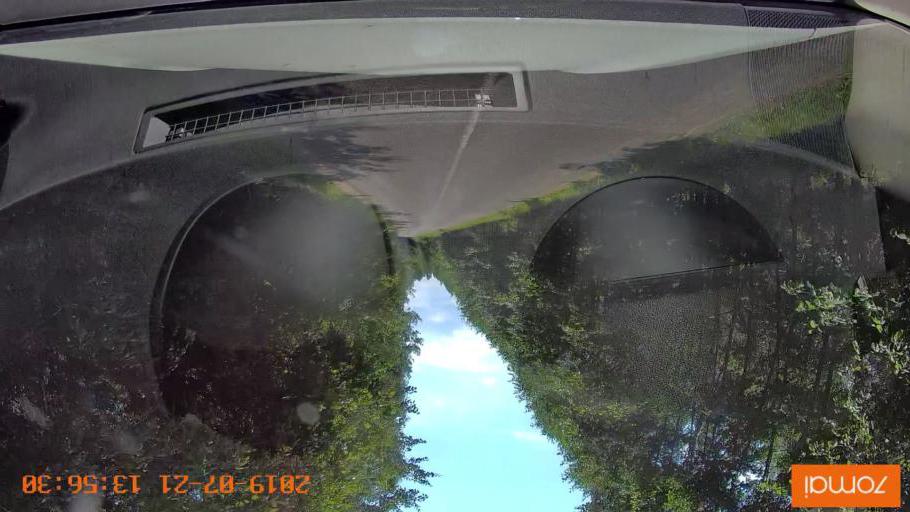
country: BY
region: Grodnenskaya
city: Lyubcha
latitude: 53.7792
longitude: 26.0996
